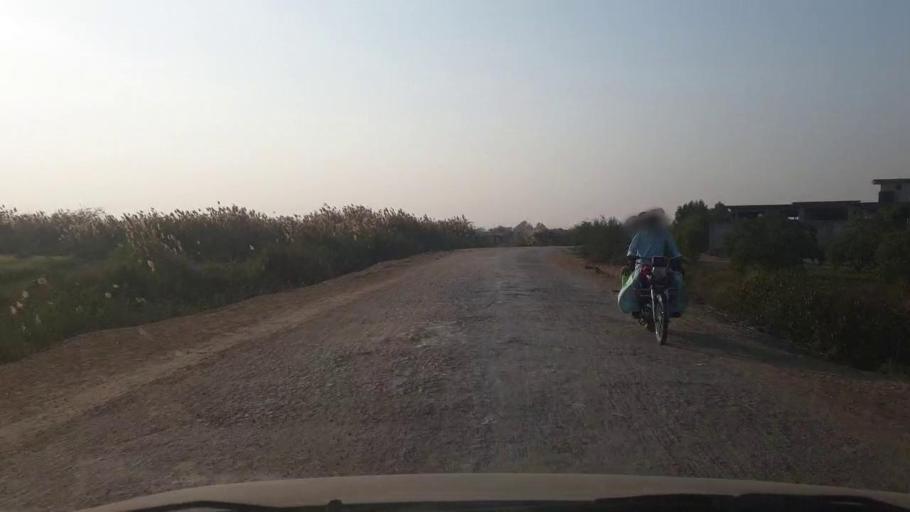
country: PK
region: Sindh
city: Mirwah Gorchani
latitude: 25.3721
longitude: 69.1276
